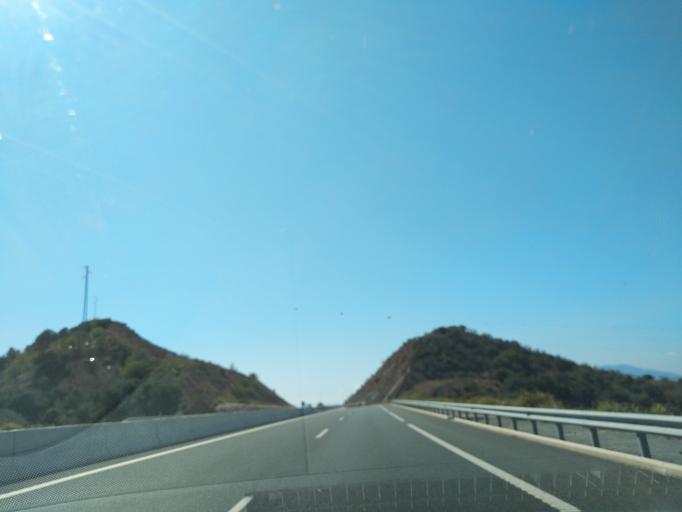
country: ES
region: Andalusia
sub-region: Provincia de Malaga
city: Almogia
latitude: 36.8249
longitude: -4.4699
